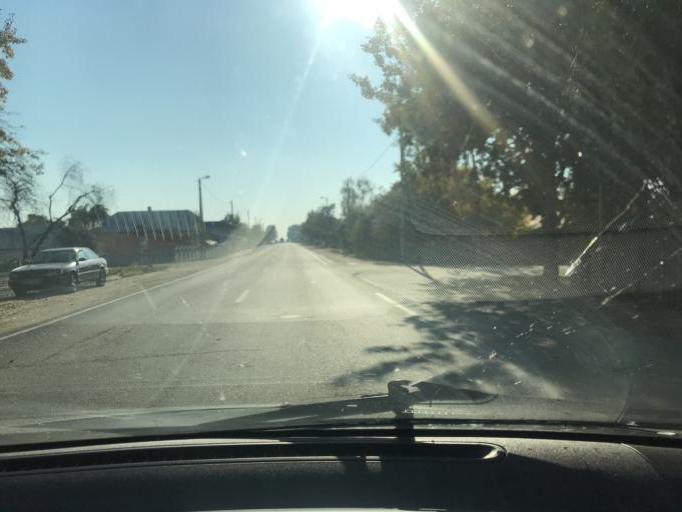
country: BY
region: Brest
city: Davyd-Haradok
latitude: 52.0751
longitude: 27.3401
